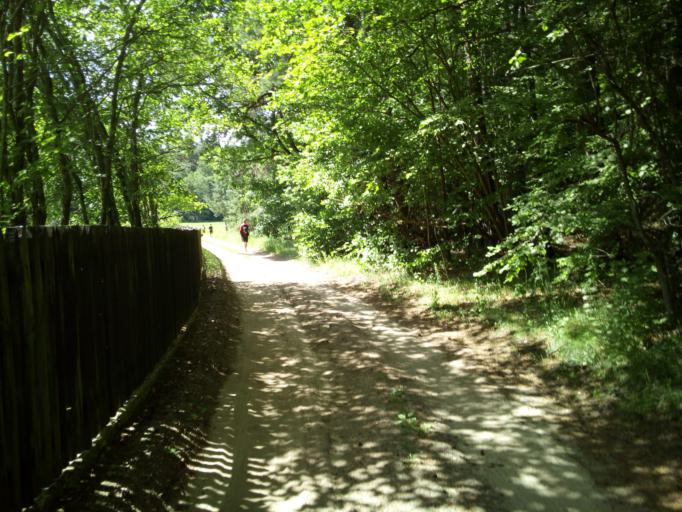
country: LT
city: Svencioneliai
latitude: 55.2755
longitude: 26.0616
